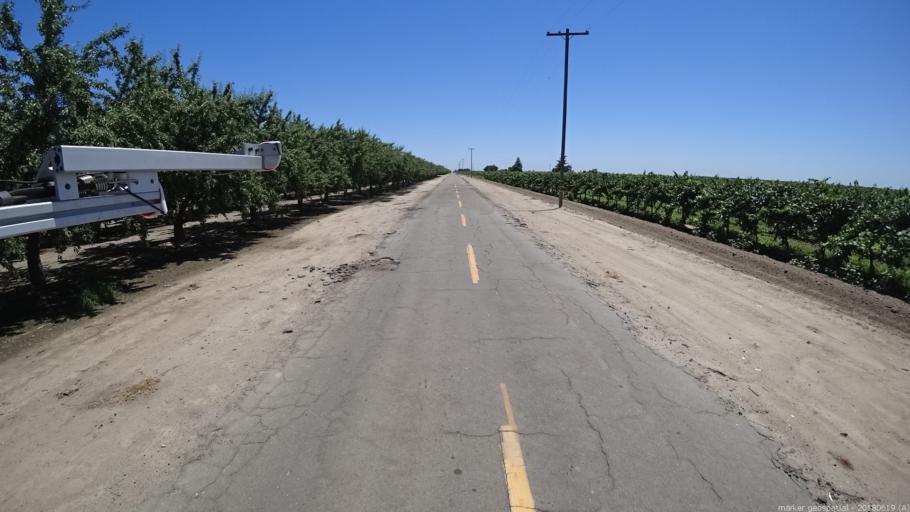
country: US
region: California
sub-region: Madera County
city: Parkwood
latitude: 36.8730
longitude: -120.1081
